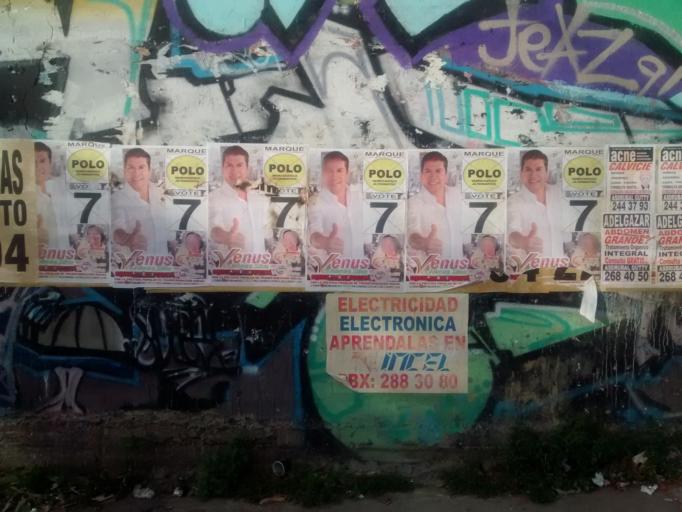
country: CO
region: Bogota D.C.
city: Bogota
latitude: 4.5871
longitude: -74.1072
